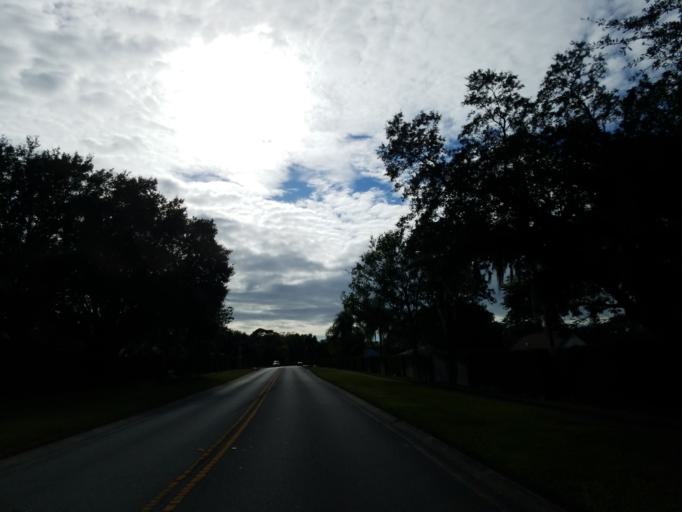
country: US
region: Florida
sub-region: Hillsborough County
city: Bloomingdale
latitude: 27.8859
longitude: -82.2592
